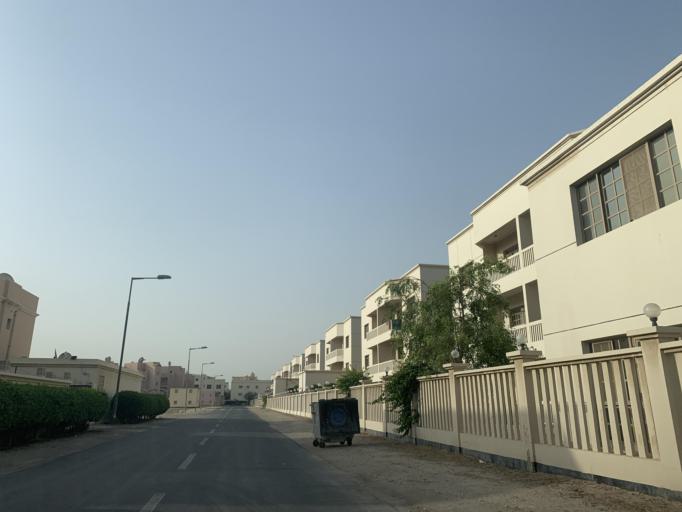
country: BH
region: Manama
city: Manama
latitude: 26.1958
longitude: 50.5643
